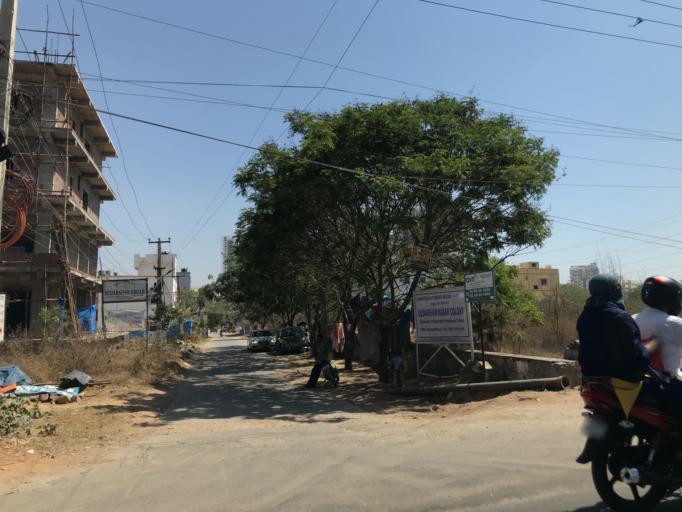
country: IN
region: Telangana
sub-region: Medak
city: Serilingampalle
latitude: 17.4694
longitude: 78.3306
